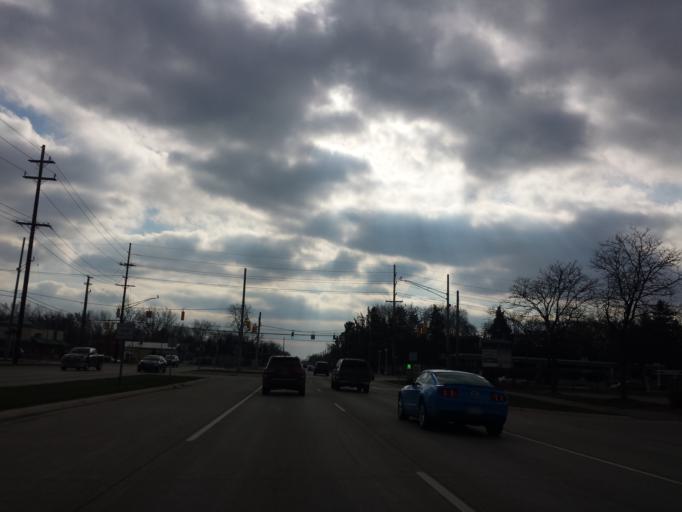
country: US
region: Michigan
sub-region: Oakland County
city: Rochester Hills
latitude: 42.6358
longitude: -83.1706
